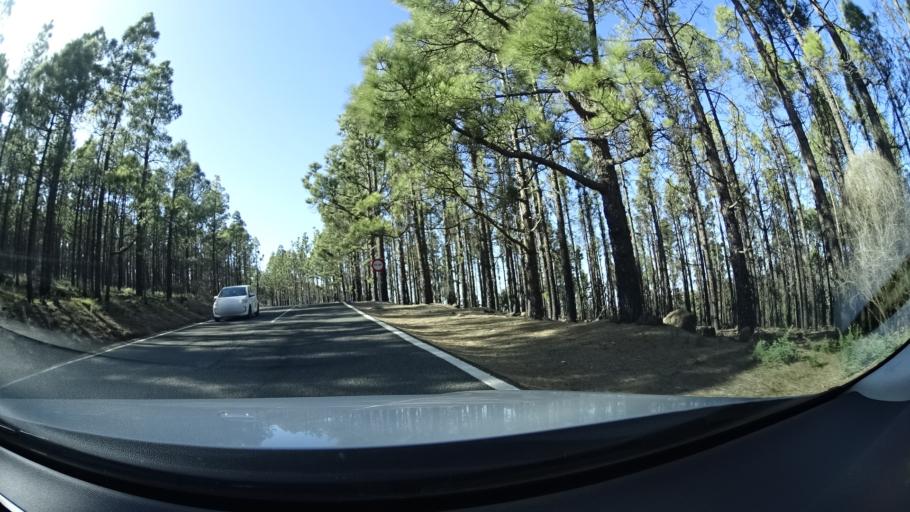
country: ES
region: Canary Islands
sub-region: Provincia de Las Palmas
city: San Bartolome
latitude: 27.9642
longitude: -15.5525
